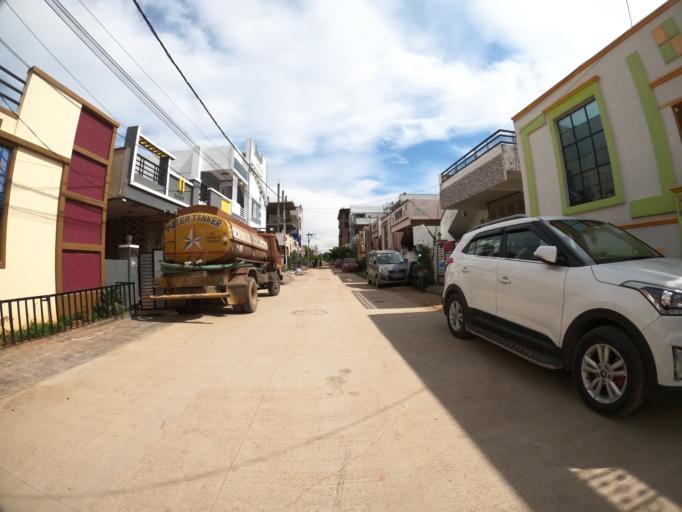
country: IN
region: Telangana
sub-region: Hyderabad
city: Hyderabad
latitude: 17.3643
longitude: 78.3834
